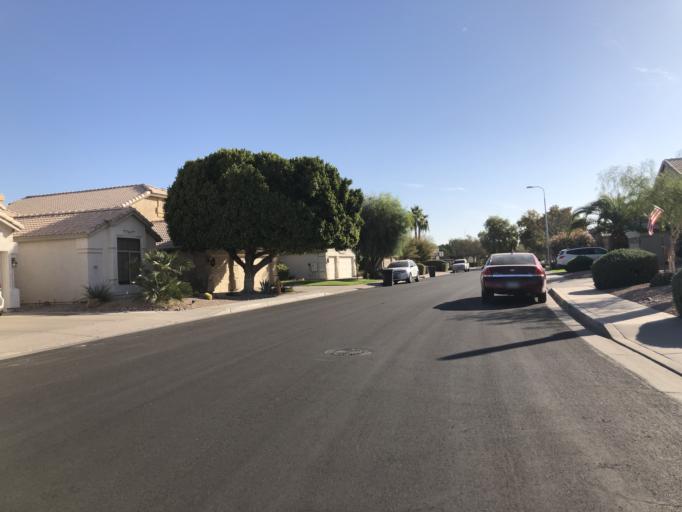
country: US
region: Arizona
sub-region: Maricopa County
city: Guadalupe
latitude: 33.3192
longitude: -111.9168
